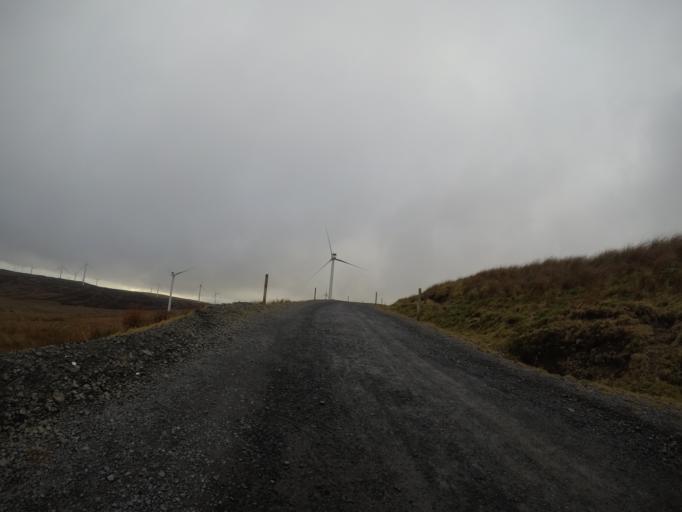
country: GB
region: Scotland
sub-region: North Ayrshire
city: Fairlie
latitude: 55.7598
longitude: -4.7923
